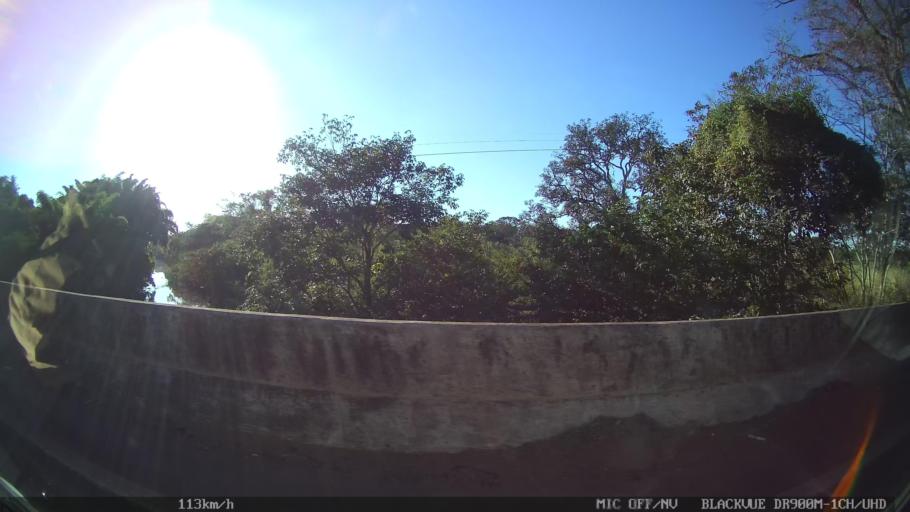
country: BR
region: Sao Paulo
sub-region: Guapiacu
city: Guapiacu
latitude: -20.7424
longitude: -49.1028
